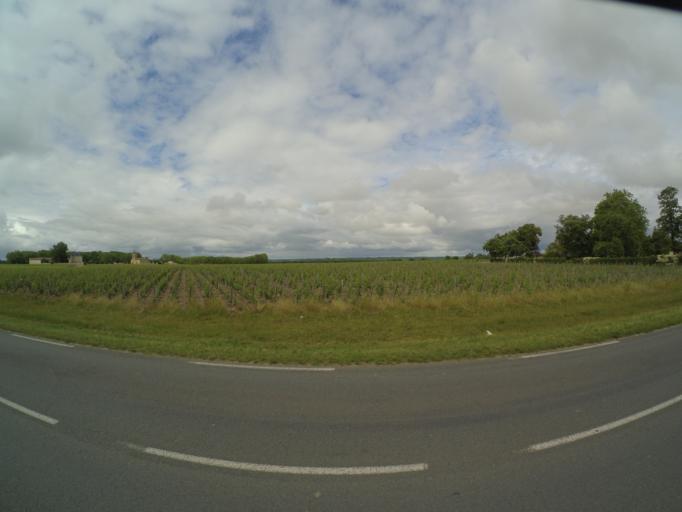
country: FR
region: Aquitaine
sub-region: Departement de la Gironde
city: Margaux
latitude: 45.0373
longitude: -0.6709
